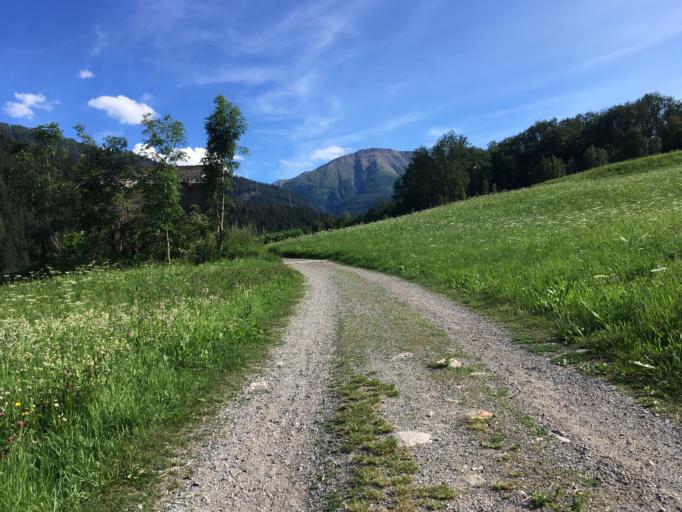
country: CH
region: Valais
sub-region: Goms District
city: Fiesch
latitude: 46.4175
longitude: 8.1406
